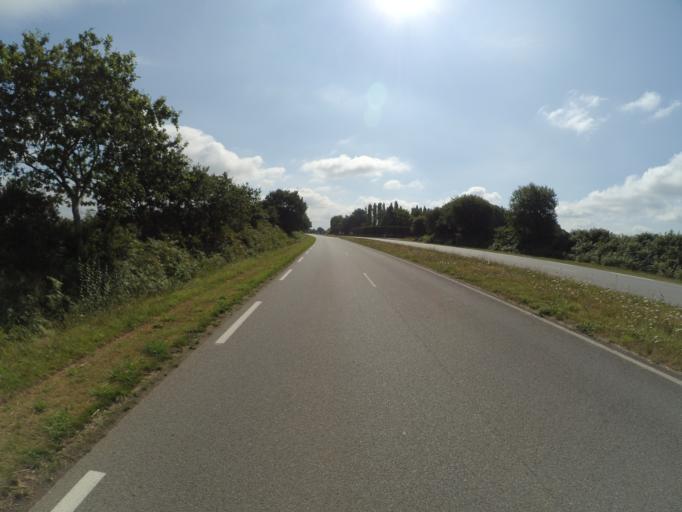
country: FR
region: Brittany
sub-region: Departement du Finistere
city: Bannalec
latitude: 47.9228
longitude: -3.6707
